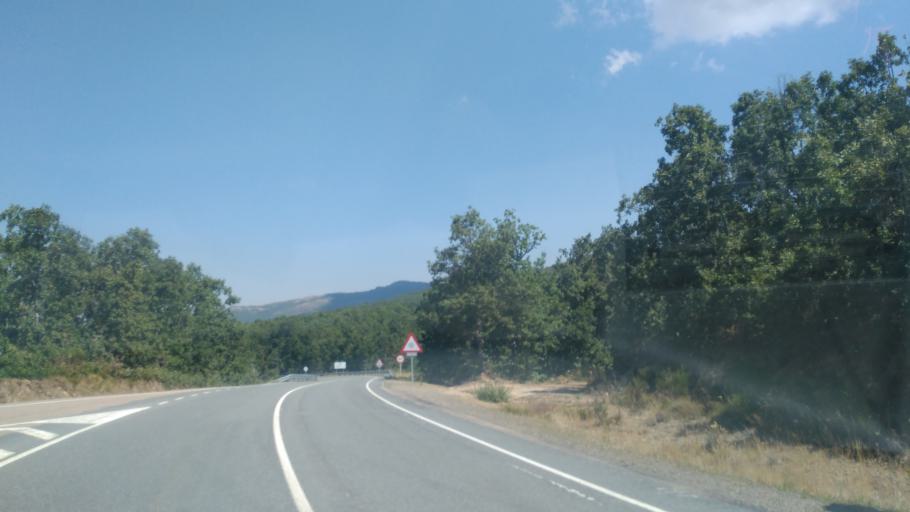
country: ES
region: Castille and Leon
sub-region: Provincia de Salamanca
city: Cilleros de la Bastida
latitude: 40.5568
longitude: -6.0677
